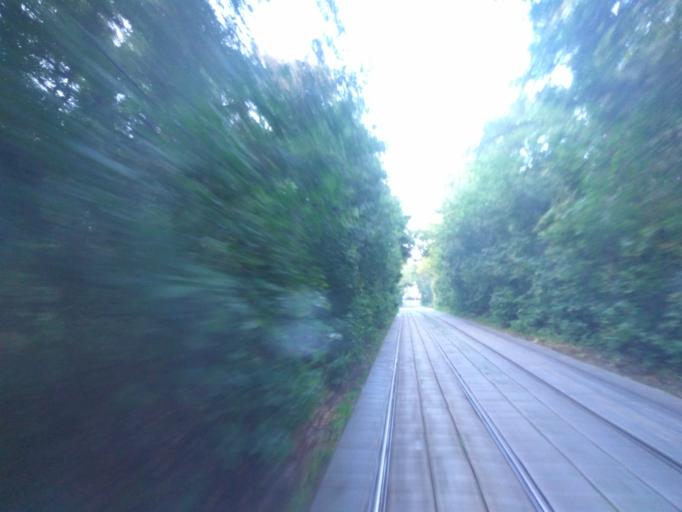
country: RU
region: Moscow
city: Sokol'niki
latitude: 55.8038
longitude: 37.6898
